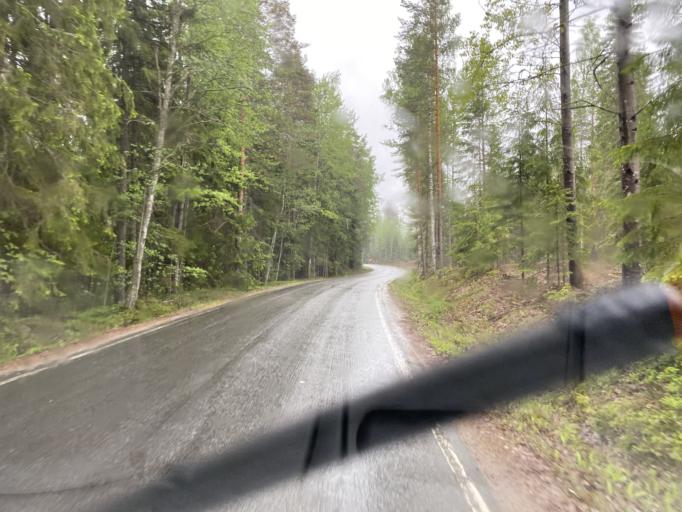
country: FI
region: Haeme
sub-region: Forssa
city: Humppila
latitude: 61.0880
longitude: 23.3092
